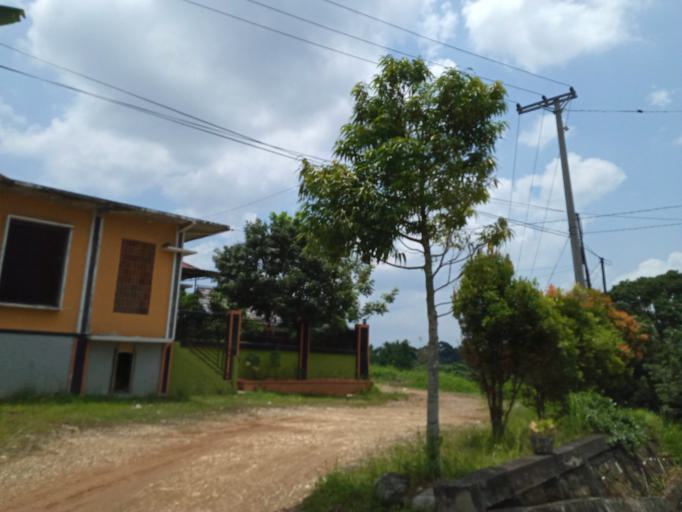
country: ID
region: Jambi
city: Bangko
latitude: -2.0857
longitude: 102.2597
